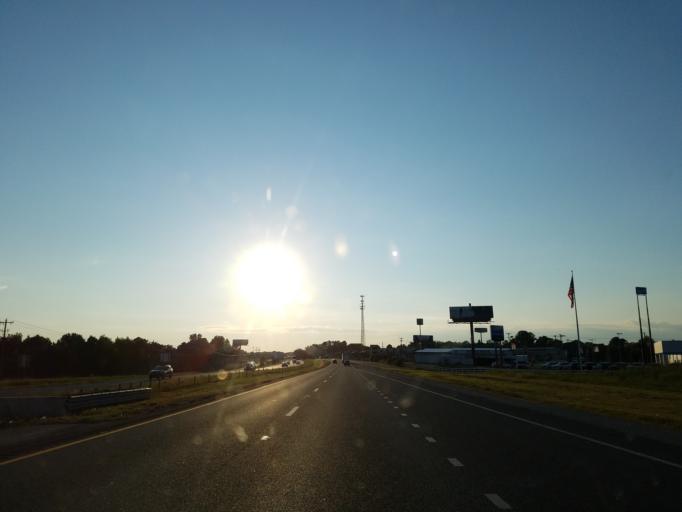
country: US
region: South Carolina
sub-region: Cherokee County
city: Gaffney
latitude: 35.0973
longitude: -81.6698
